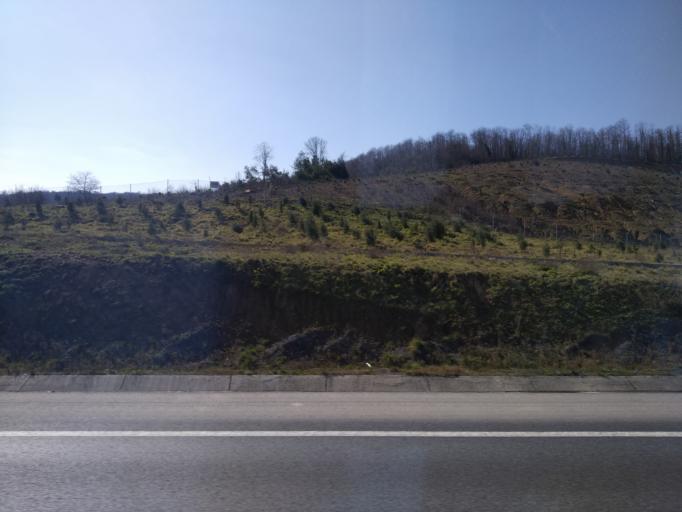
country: TR
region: Istanbul
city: Mahmut Sevket Pasa
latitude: 41.1657
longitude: 29.2548
